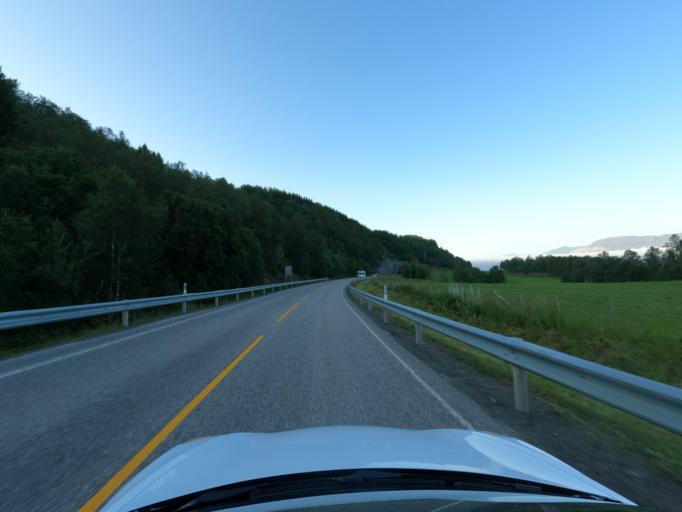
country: NO
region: Troms
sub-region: Harstad
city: Harstad
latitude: 68.7288
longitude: 16.5426
